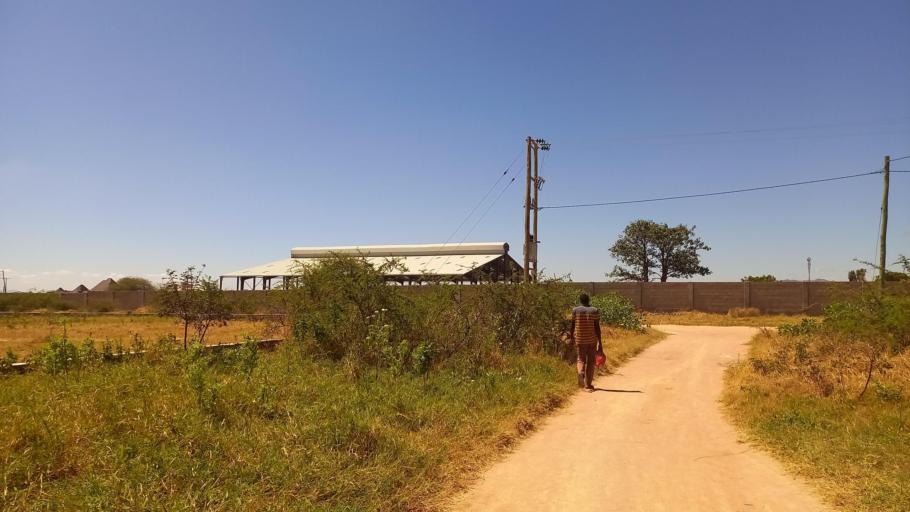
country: TZ
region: Dodoma
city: Dodoma
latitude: -6.1408
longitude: 35.6956
